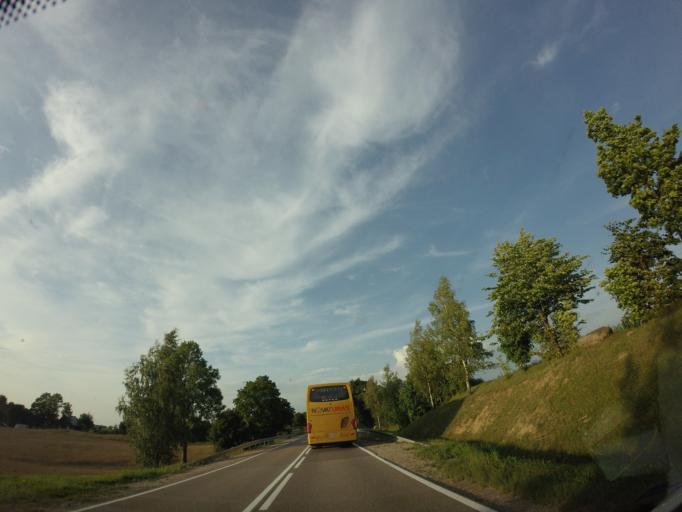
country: PL
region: Podlasie
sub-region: Powiat sejnenski
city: Sejny
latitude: 54.1038
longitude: 23.4061
